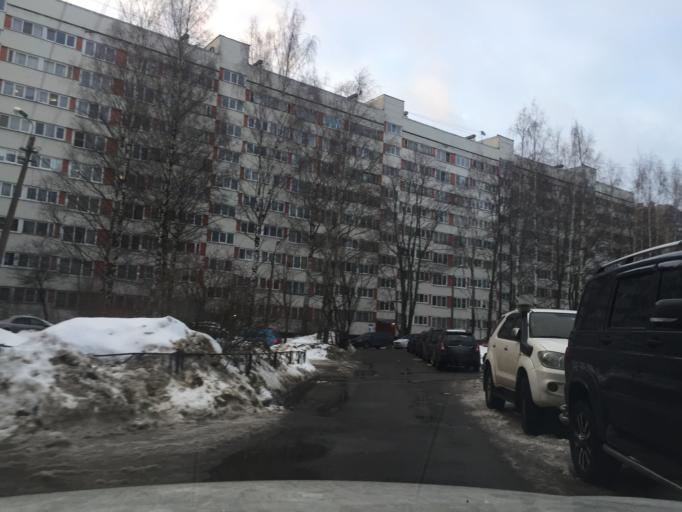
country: RU
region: St.-Petersburg
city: Grazhdanka
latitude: 60.0327
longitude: 30.4093
